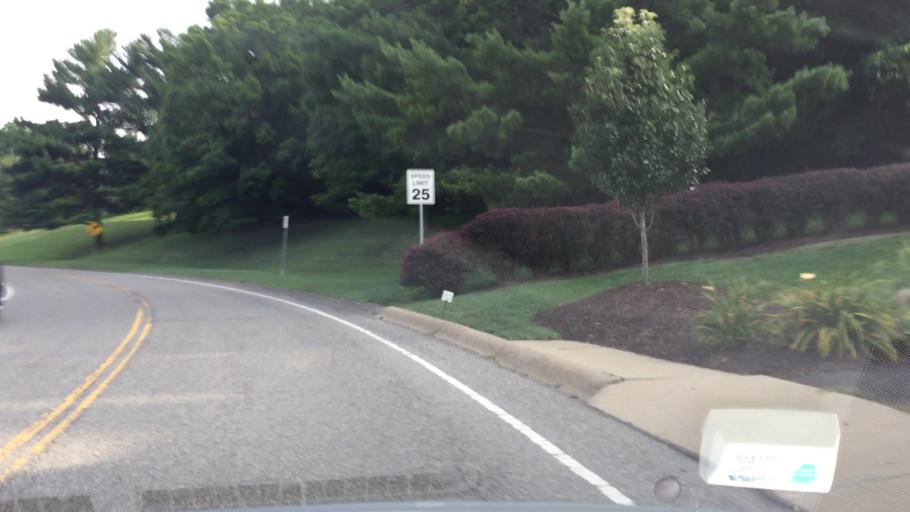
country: US
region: Pennsylvania
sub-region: Allegheny County
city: Heidelberg
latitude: 40.3724
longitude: -80.0877
